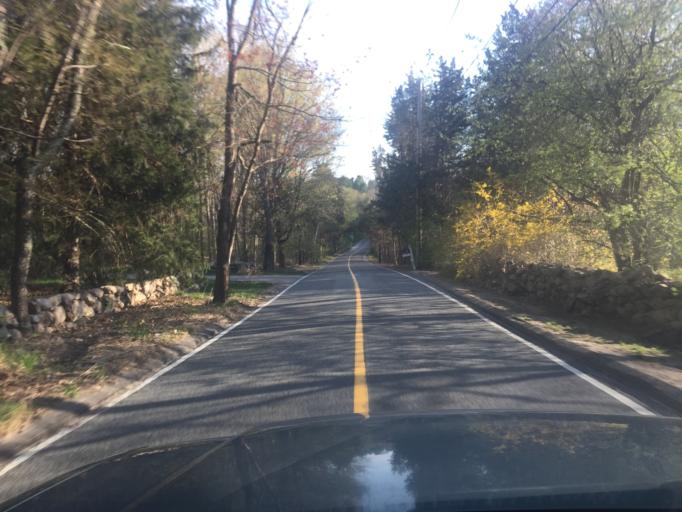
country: US
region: Massachusetts
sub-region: Middlesex County
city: Sherborn
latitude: 42.2238
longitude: -71.3545
